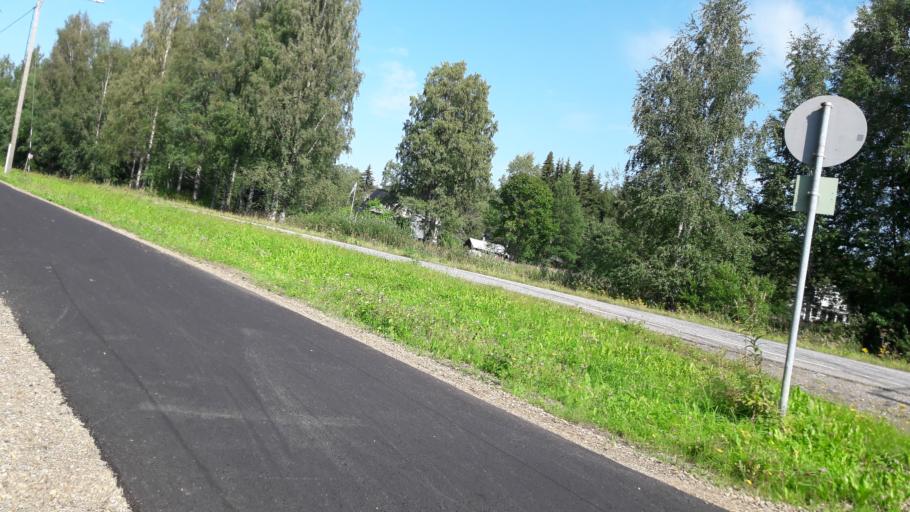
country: FI
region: North Karelia
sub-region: Joensuu
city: Joensuu
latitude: 62.5329
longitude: 29.8499
